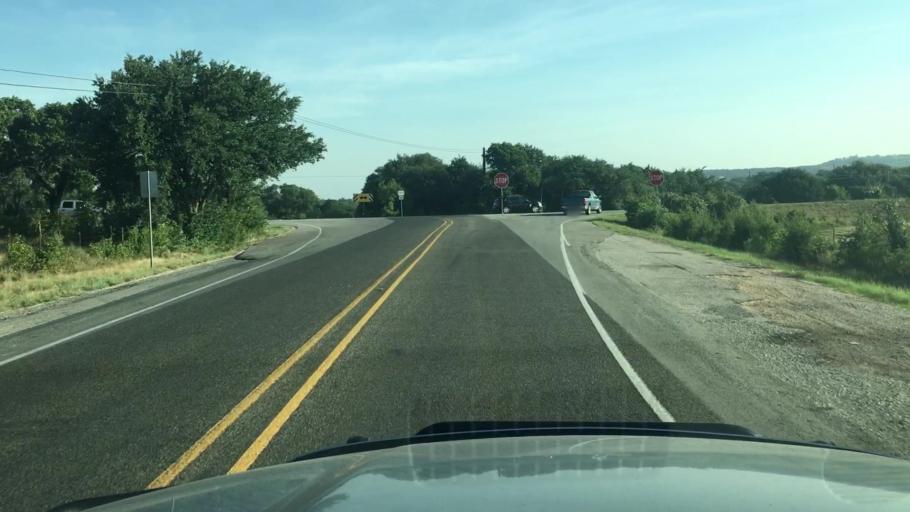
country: US
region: Texas
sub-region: Hays County
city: Dripping Springs
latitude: 30.1926
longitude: -98.2150
